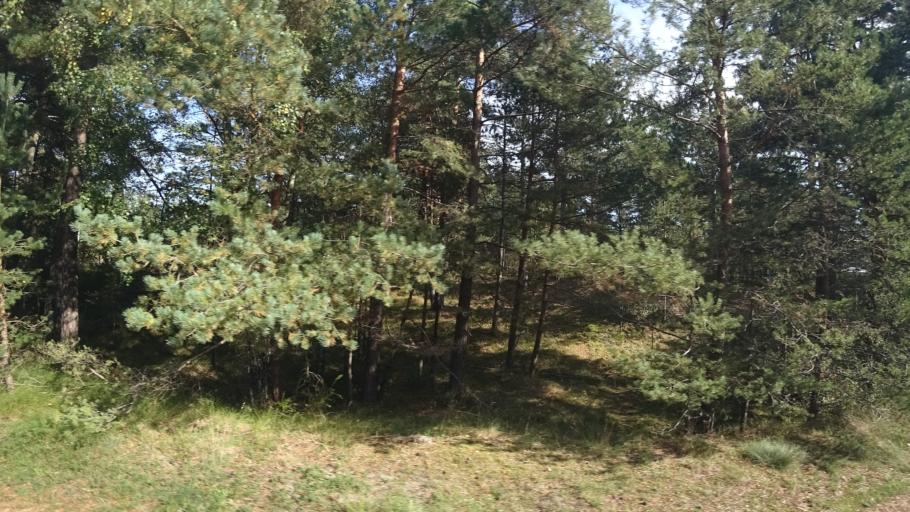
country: SE
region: Skane
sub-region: Kristianstads Kommun
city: Ahus
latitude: 55.9117
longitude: 14.2874
